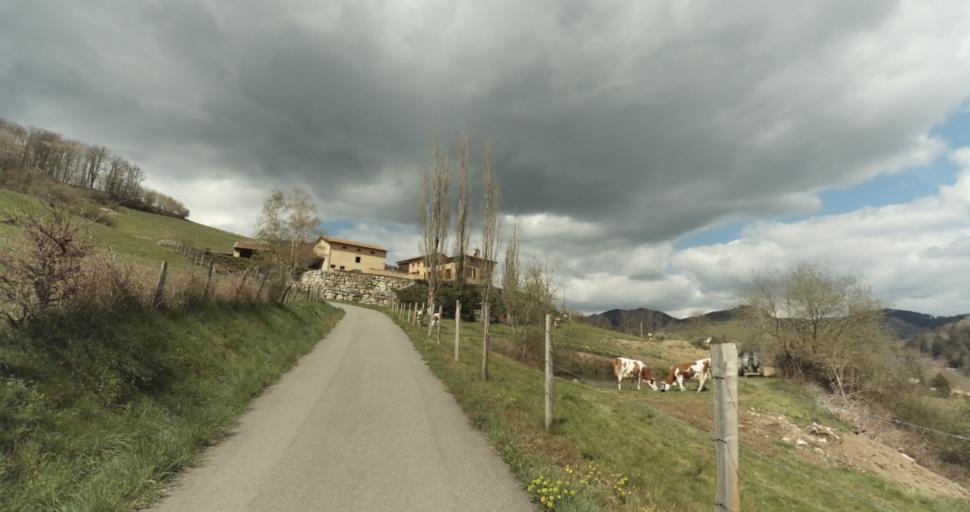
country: FR
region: Rhone-Alpes
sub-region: Departement du Rhone
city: Tarare
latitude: 45.9045
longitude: 4.4283
